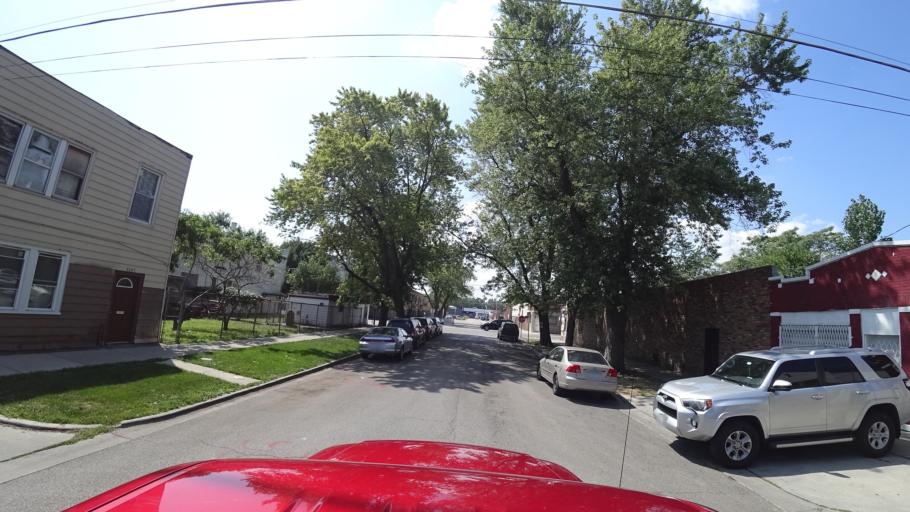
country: US
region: Illinois
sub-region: Cook County
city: Chicago
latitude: 41.8088
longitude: -87.6918
